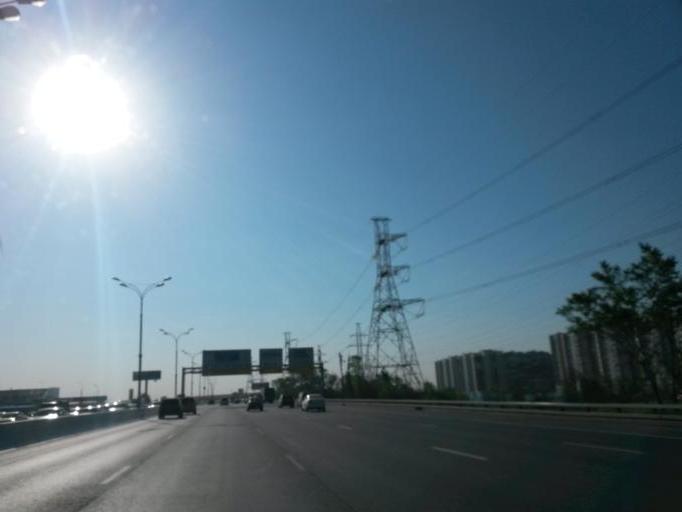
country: RU
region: Moscow
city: Chertanovo Yuzhnoye
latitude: 55.5785
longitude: 37.5829
